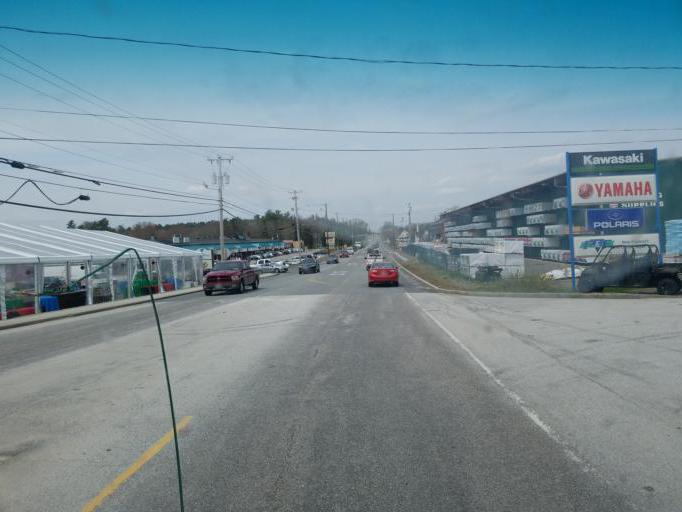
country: US
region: Maine
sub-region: Hancock County
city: Ellsworth
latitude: 44.5507
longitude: -68.4273
